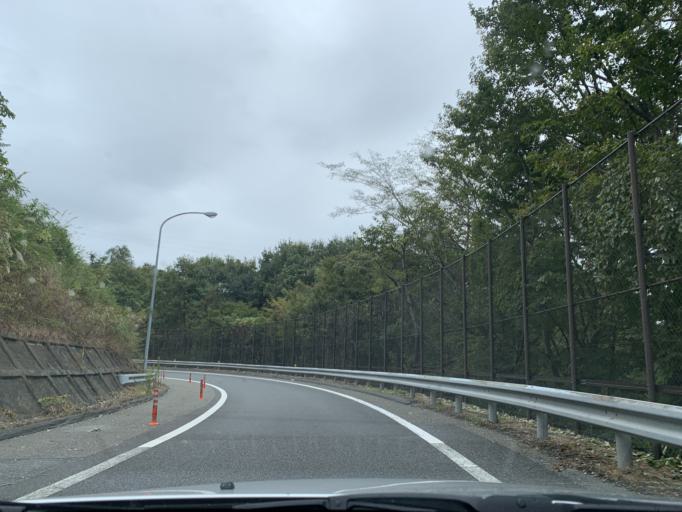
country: JP
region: Shizuoka
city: Gotemba
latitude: 35.3573
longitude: 139.0141
